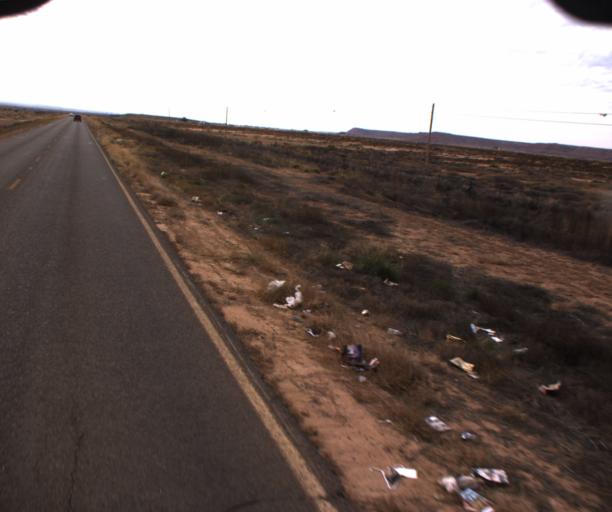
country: US
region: Arizona
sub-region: Apache County
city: Many Farms
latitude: 36.3223
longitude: -109.6173
